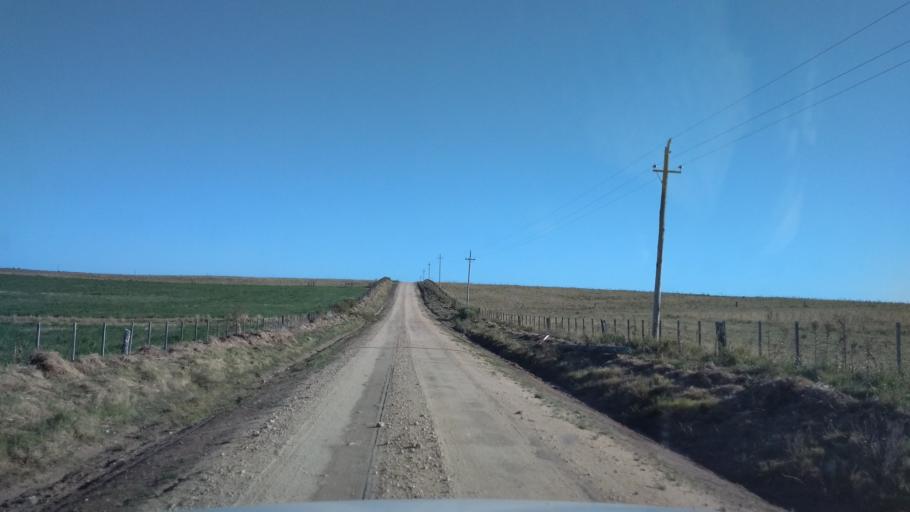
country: UY
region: Florida
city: Casupa
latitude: -34.0087
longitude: -55.7871
